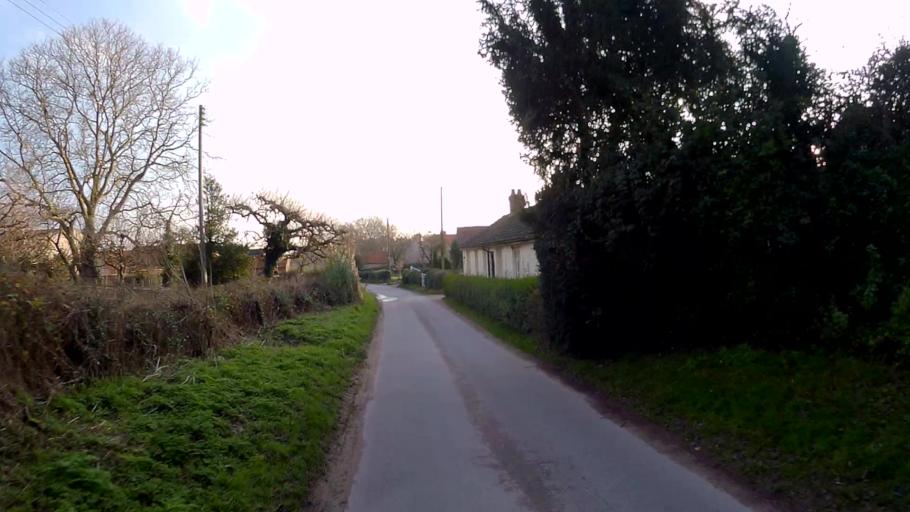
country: GB
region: England
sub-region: Lincolnshire
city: Bourne
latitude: 52.8040
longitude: -0.3925
